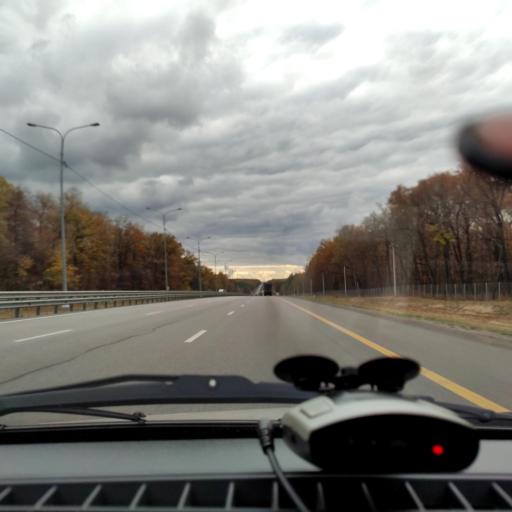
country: RU
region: Voronezj
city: Ramon'
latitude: 51.8788
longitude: 39.2168
